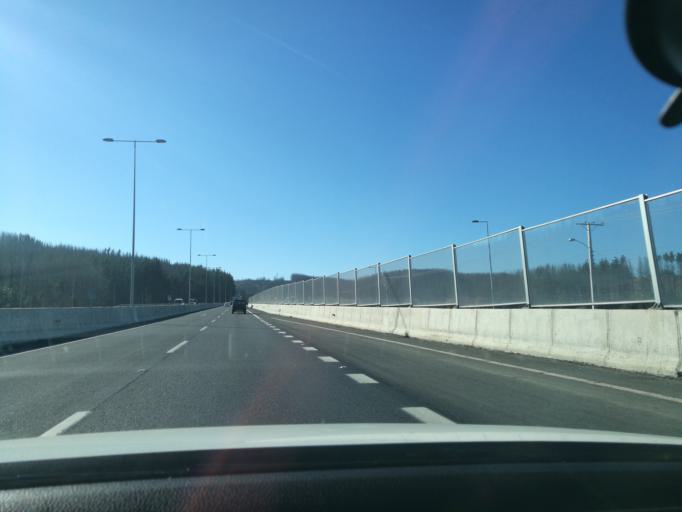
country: CL
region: Biobio
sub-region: Provincia de Concepcion
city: Penco
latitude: -36.8562
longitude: -72.8738
